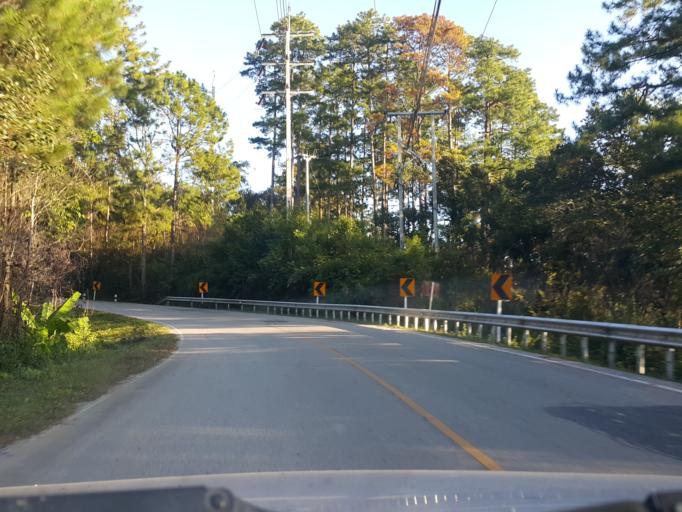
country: TH
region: Mae Hong Son
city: Mae Hi
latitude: 19.2673
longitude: 98.5881
